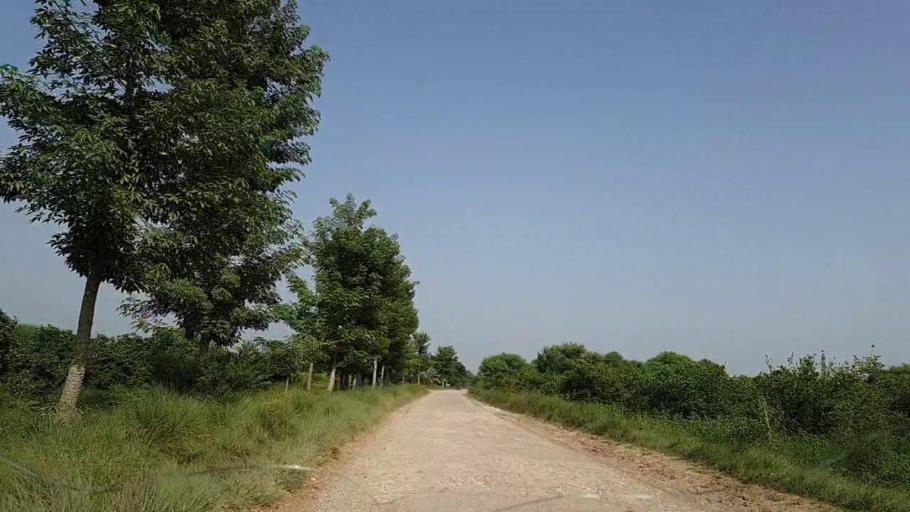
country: PK
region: Sindh
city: Kandiaro
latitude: 27.0665
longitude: 68.1790
